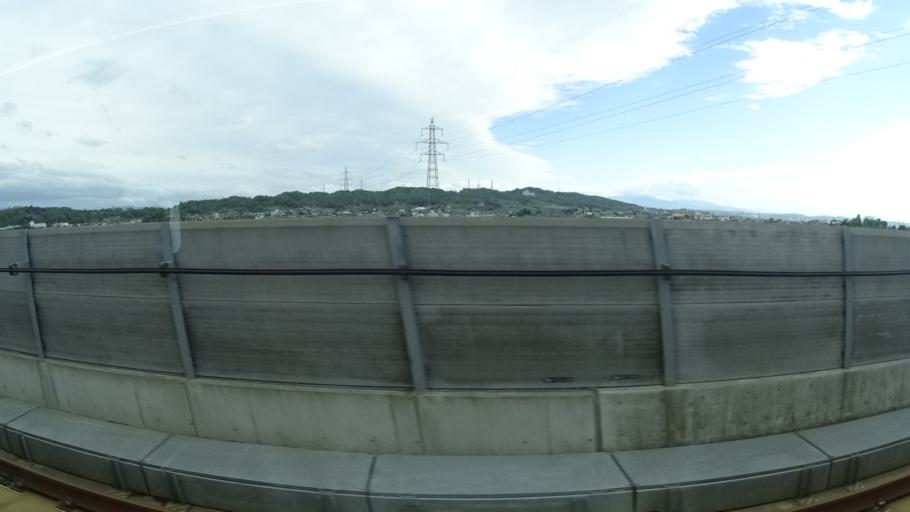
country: JP
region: Toyama
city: Kuragaki-kosugi
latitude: 36.7196
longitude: 137.1736
